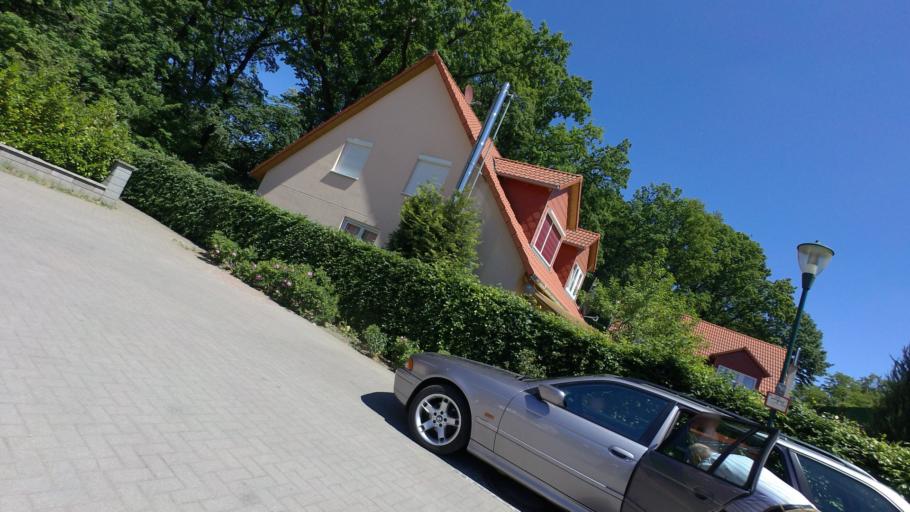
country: DE
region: Berlin
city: Reinickendorf
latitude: 52.5782
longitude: 13.3258
